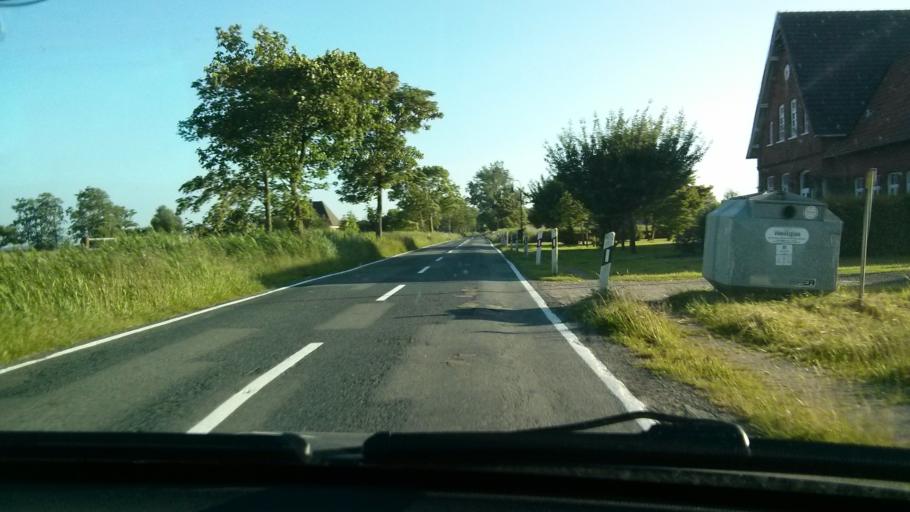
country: DE
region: Lower Saxony
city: Nordenham
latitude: 53.4733
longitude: 8.5459
